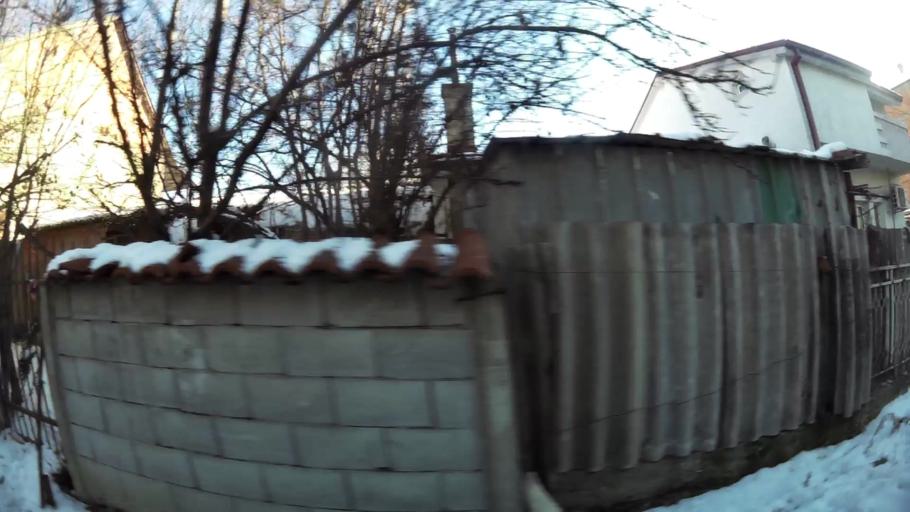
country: MK
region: Saraj
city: Saraj
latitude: 42.0082
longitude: 21.3348
